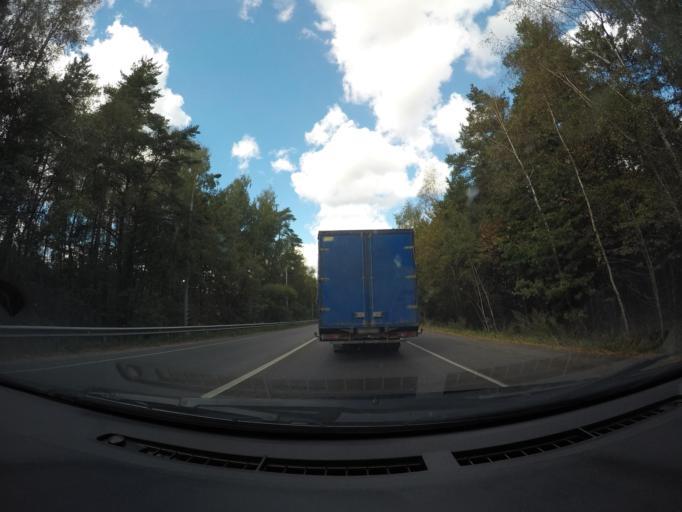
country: RU
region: Moskovskaya
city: Il'inskiy
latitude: 55.6475
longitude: 38.1351
